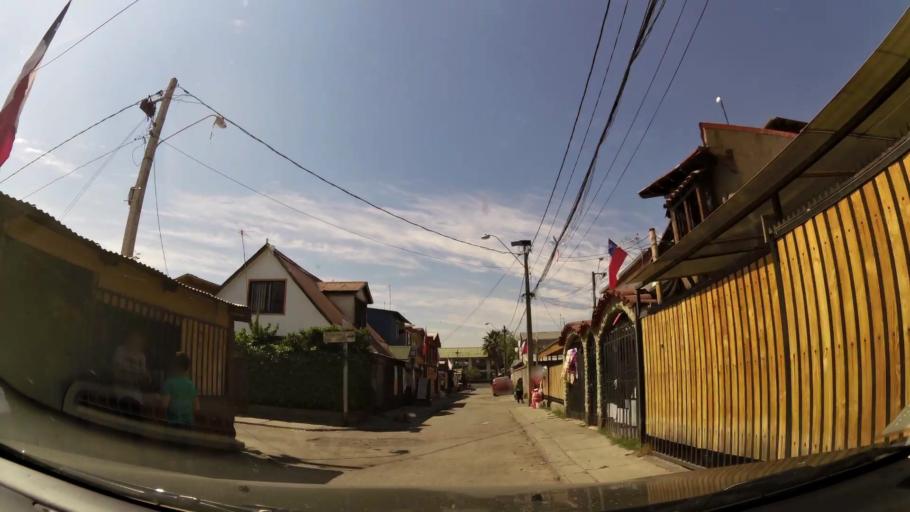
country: CL
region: Santiago Metropolitan
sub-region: Provincia de Santiago
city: La Pintana
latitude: -33.5889
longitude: -70.6174
